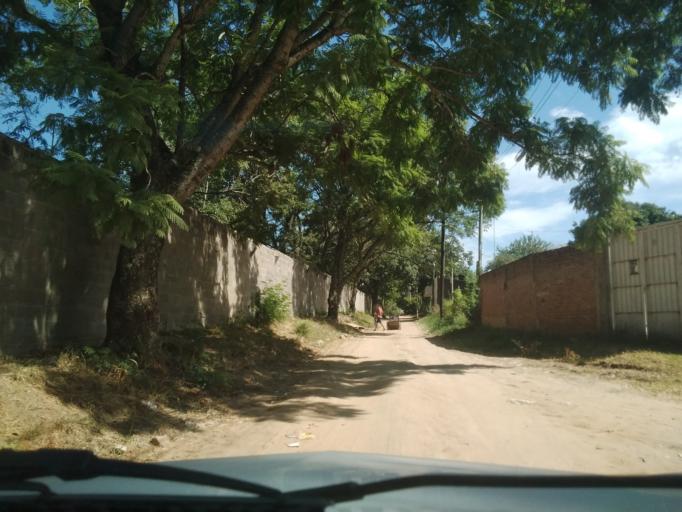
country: AR
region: Corrientes
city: Corrientes
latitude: -27.5125
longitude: -58.8058
